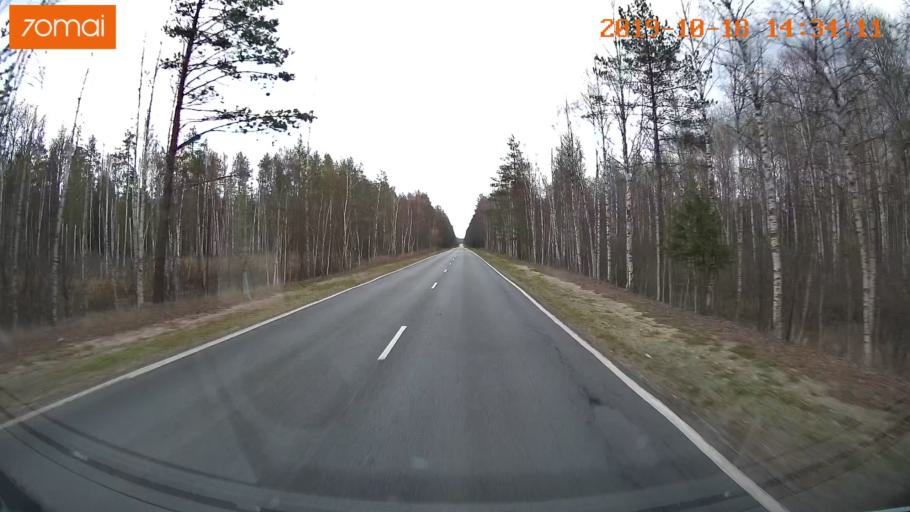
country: RU
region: Vladimir
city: Velikodvorskiy
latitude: 55.2095
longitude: 40.6112
